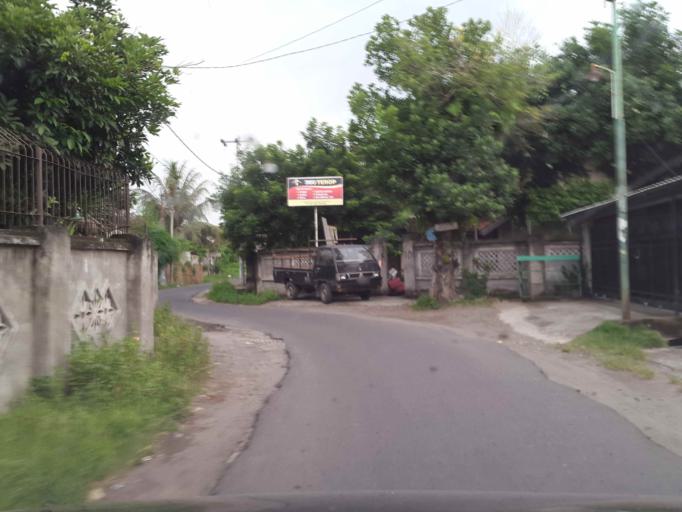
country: ID
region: West Nusa Tenggara
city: Kekeri
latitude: -8.5556
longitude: 116.1137
